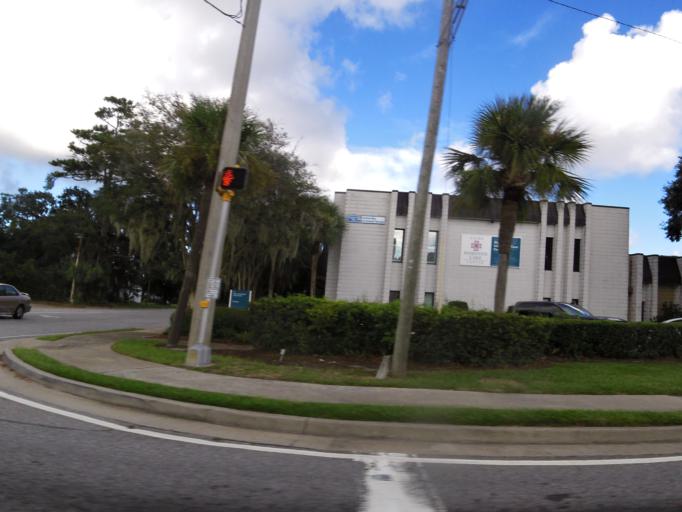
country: US
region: Georgia
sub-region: Glynn County
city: Brunswick
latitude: 31.1722
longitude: -81.4741
